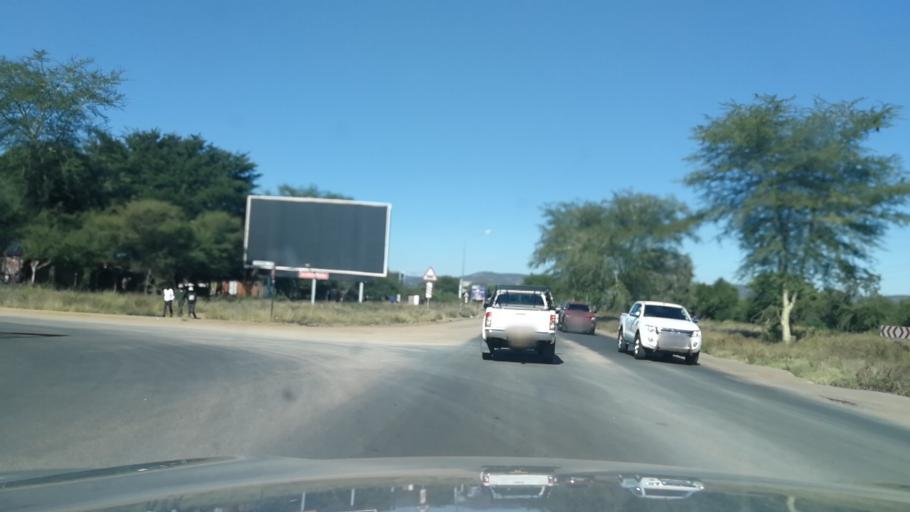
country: BW
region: South East
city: Gaborone
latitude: -24.6906
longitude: 25.8877
